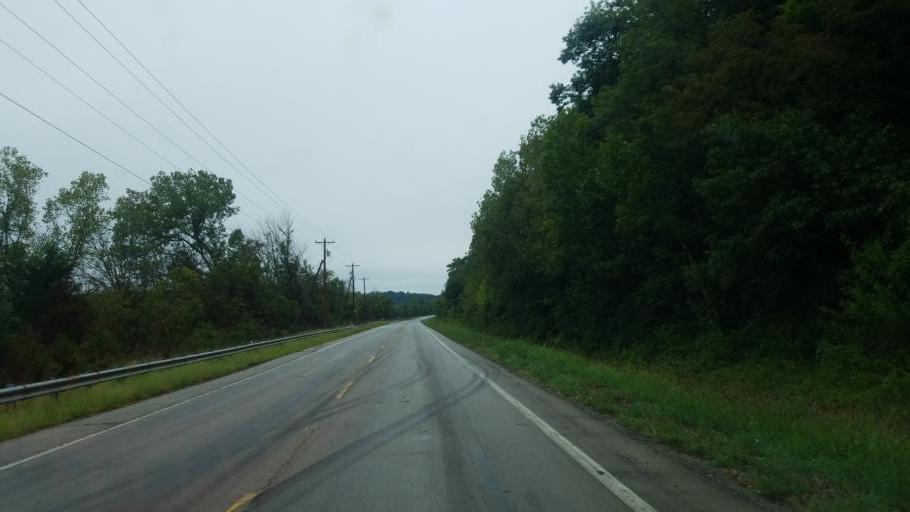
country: US
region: Kentucky
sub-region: Mason County
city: Maysville
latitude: 38.6491
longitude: -83.7326
